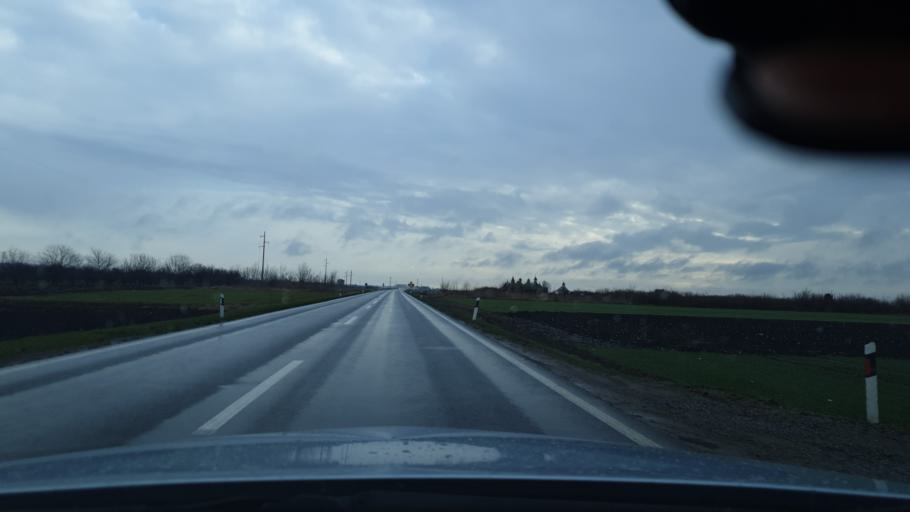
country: RS
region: Autonomna Pokrajina Vojvodina
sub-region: Juznobanatski Okrug
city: Kovin
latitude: 44.8093
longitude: 20.8670
